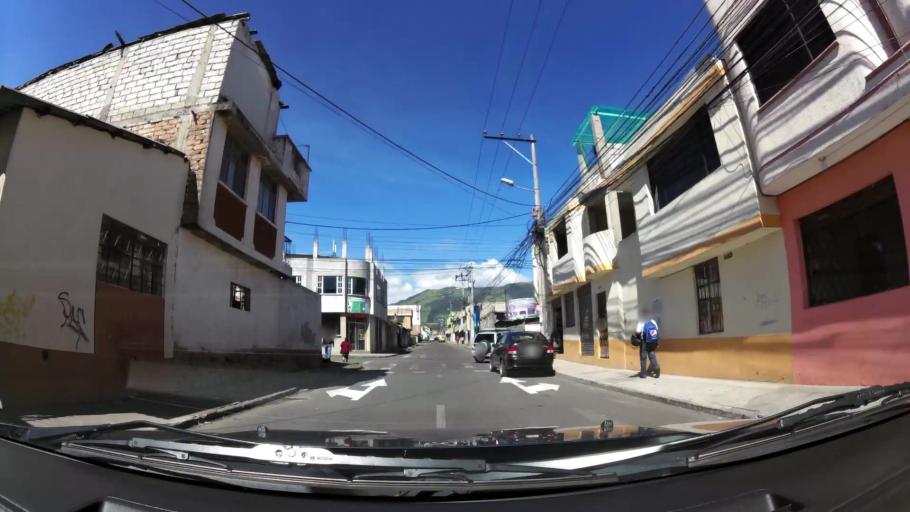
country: EC
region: Pichincha
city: Quito
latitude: -0.2783
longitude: -78.5562
